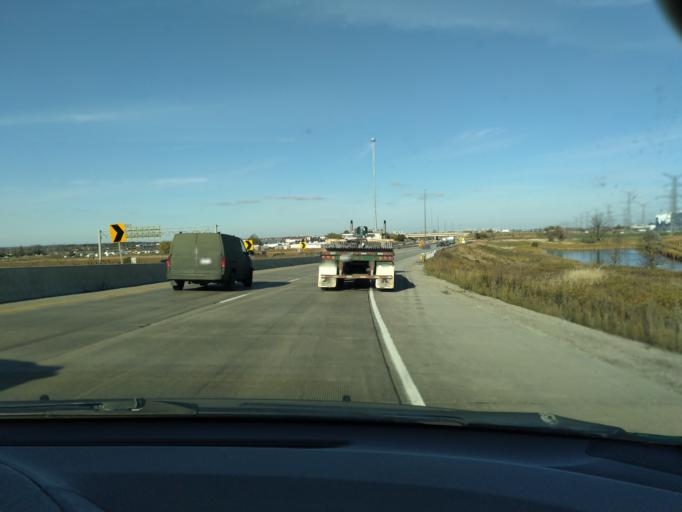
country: CA
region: Ontario
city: Brampton
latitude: 43.5987
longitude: -79.7986
